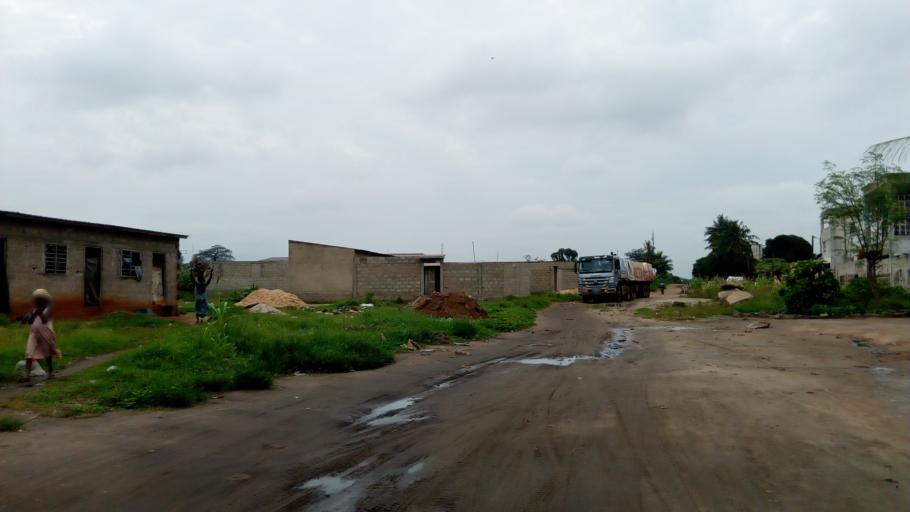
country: TG
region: Maritime
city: Lome
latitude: 6.1652
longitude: 1.2094
